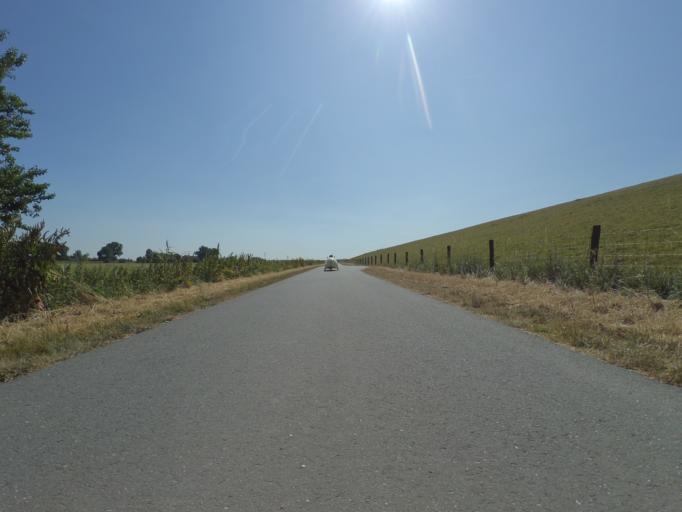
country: NL
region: Zeeland
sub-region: Gemeente Reimerswaal
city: Yerseke
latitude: 51.4095
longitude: 4.0943
